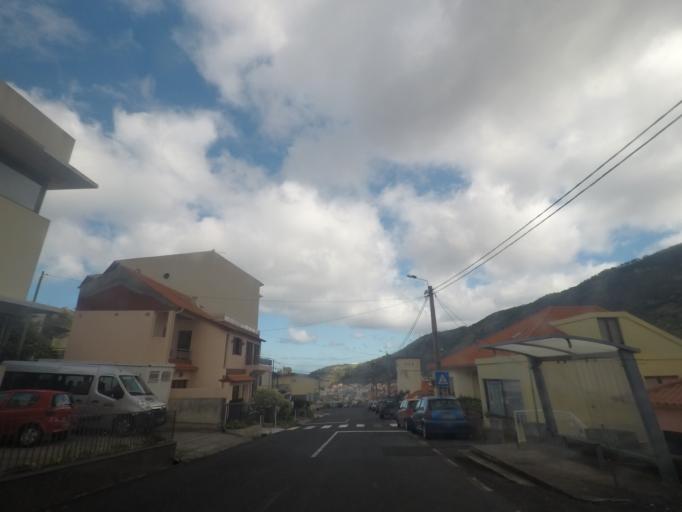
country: PT
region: Madeira
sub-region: Machico
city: Machico
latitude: 32.7315
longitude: -16.7739
